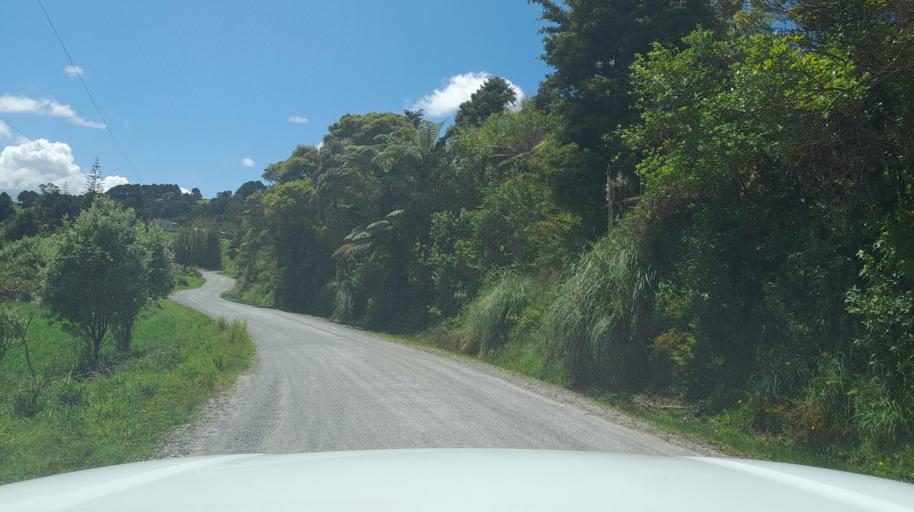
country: NZ
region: Northland
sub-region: Far North District
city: Taipa
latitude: -35.1245
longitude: 173.4085
